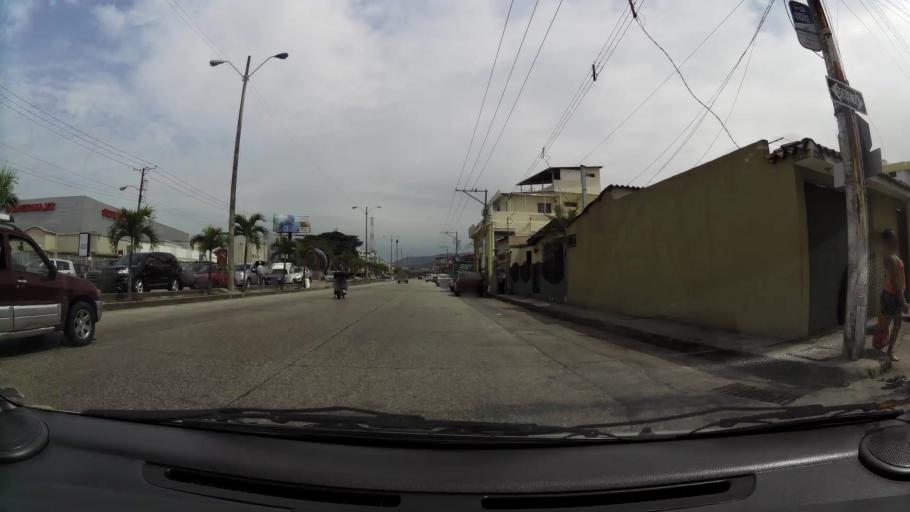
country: EC
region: Guayas
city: Eloy Alfaro
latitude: -2.1448
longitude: -79.8956
